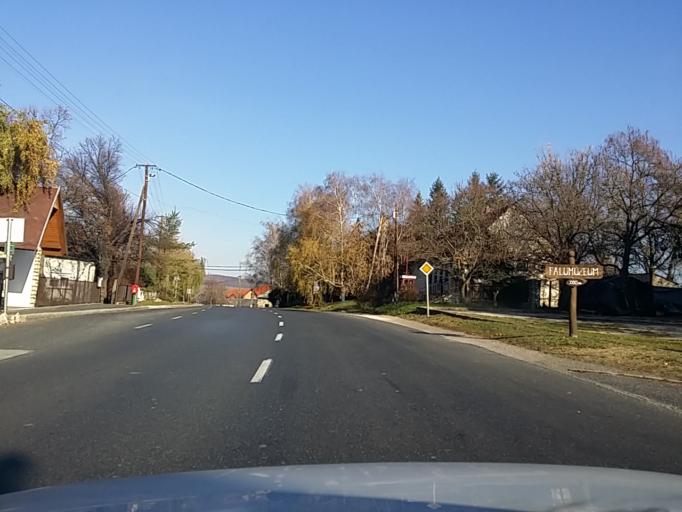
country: HU
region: Veszprem
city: Tapolca
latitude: 46.9220
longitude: 17.5508
